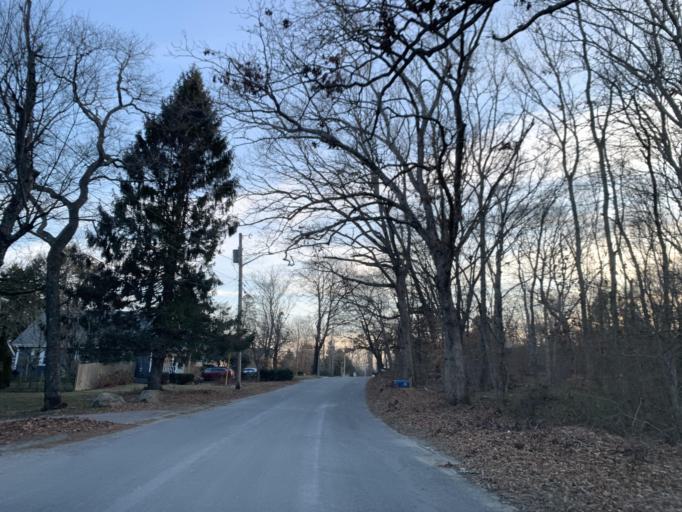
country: US
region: Rhode Island
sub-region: Washington County
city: Wakefield-Peacedale
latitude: 41.4476
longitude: -71.5069
